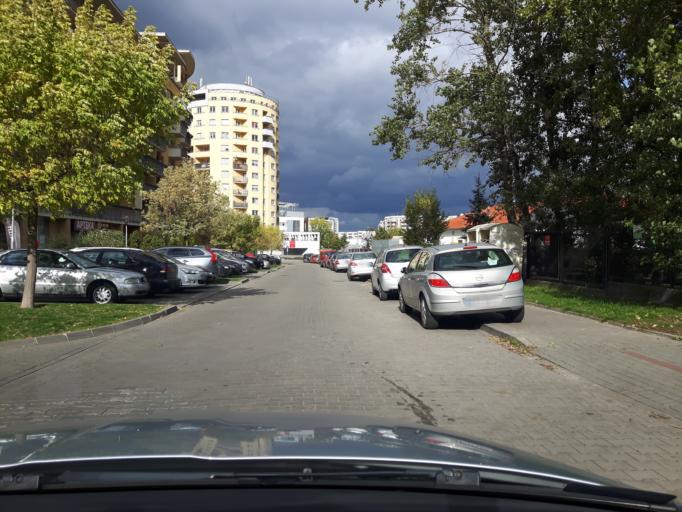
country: PL
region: Masovian Voivodeship
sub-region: Warszawa
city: Ursynow
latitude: 52.1438
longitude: 21.0363
